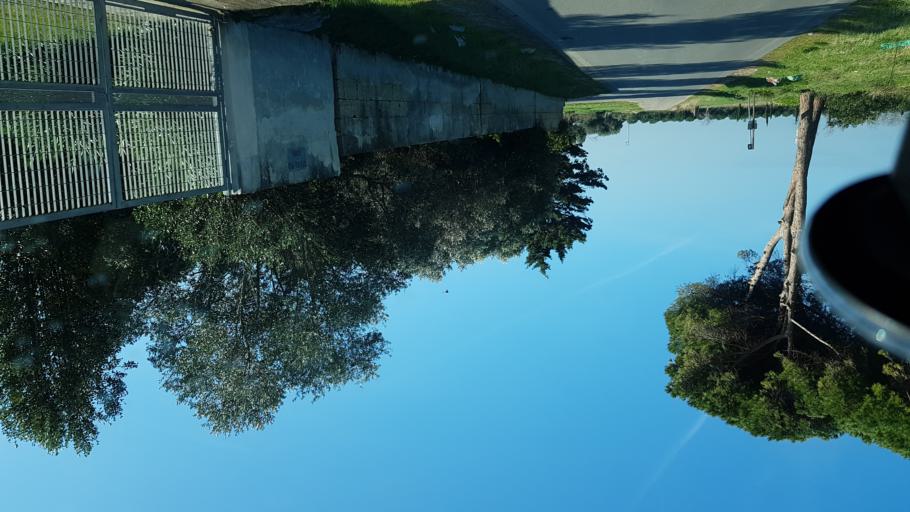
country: IT
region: Apulia
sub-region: Provincia di Brindisi
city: Brindisi
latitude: 40.6573
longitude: 17.9042
